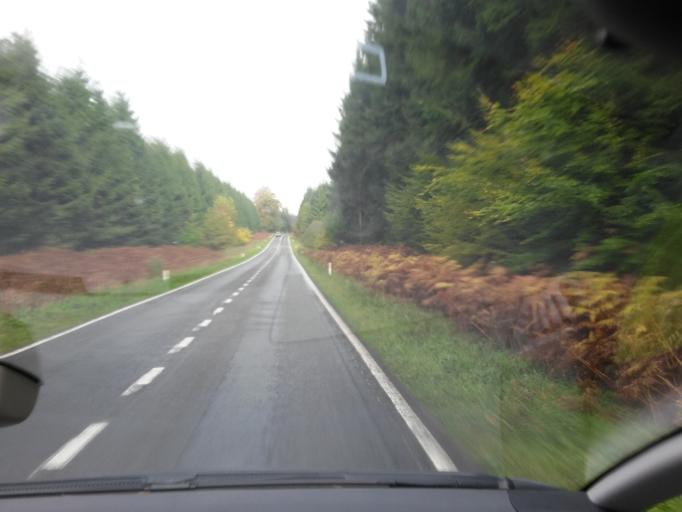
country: BE
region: Wallonia
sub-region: Province du Luxembourg
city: Chiny
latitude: 49.7550
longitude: 5.3596
